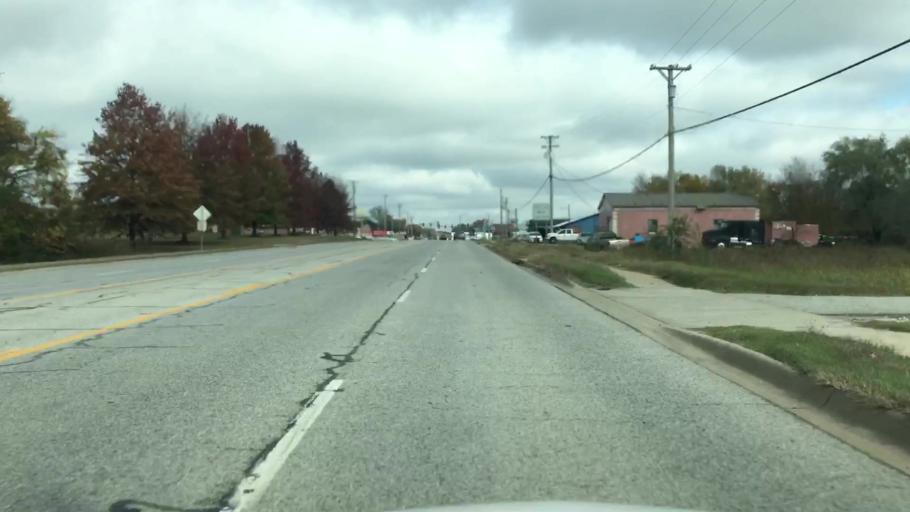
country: US
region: Arkansas
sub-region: Benton County
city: Gentry
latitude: 36.2613
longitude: -94.4836
